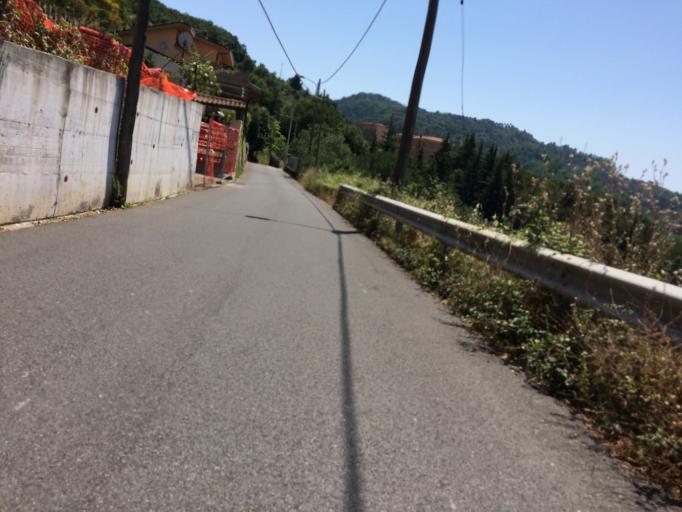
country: IT
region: Tuscany
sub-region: Provincia di Massa-Carrara
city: Carrara
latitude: 44.0757
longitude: 10.1103
